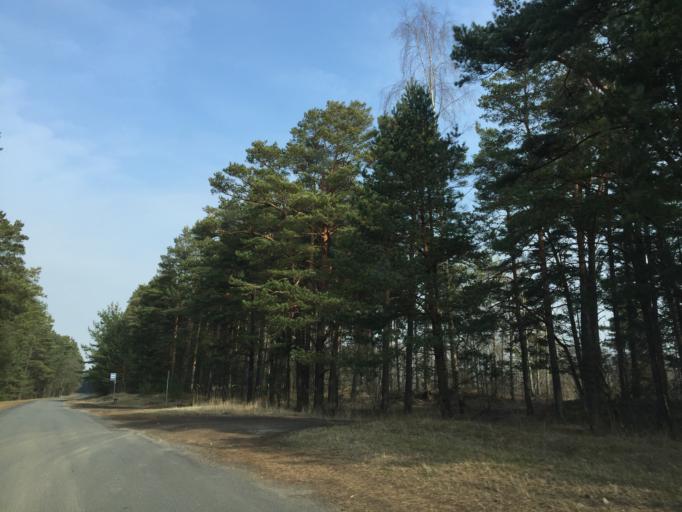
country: LV
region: Salacgrivas
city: Ainazi
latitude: 57.8893
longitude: 24.3688
